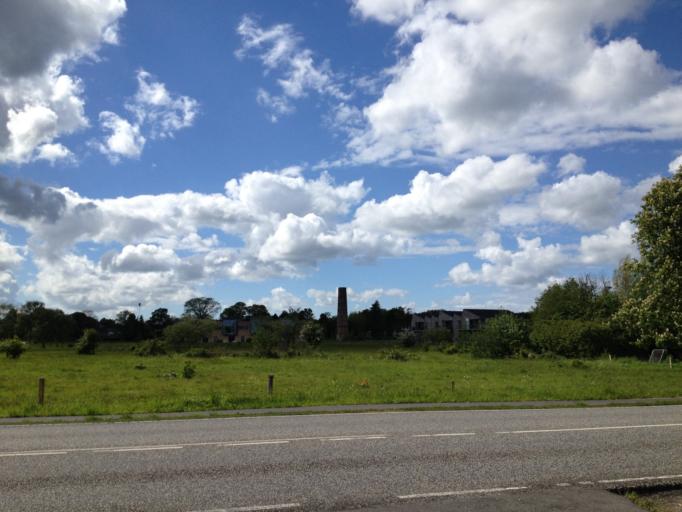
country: DK
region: Capital Region
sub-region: Fredensborg Kommune
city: Niva
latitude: 55.9369
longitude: 12.5233
